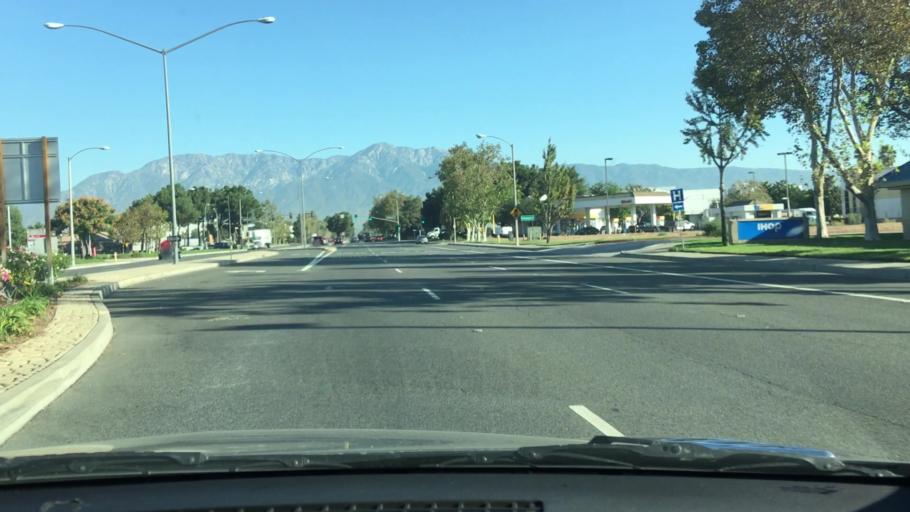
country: US
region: California
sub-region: San Bernardino County
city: Ontario
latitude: 34.0319
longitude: -117.5931
